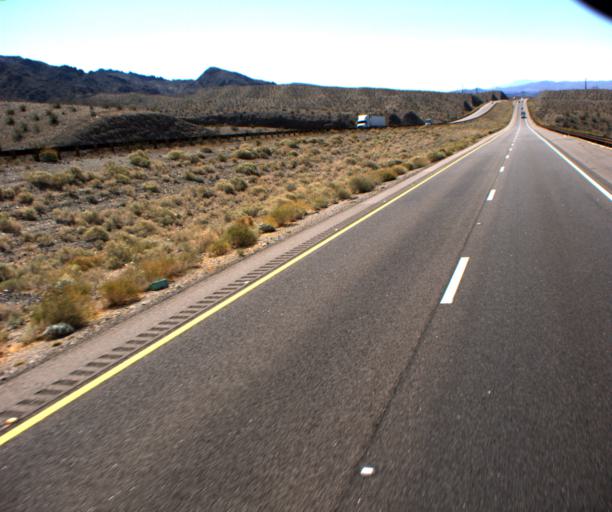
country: US
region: Nevada
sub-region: Clark County
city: Boulder City
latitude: 35.9238
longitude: -114.6327
